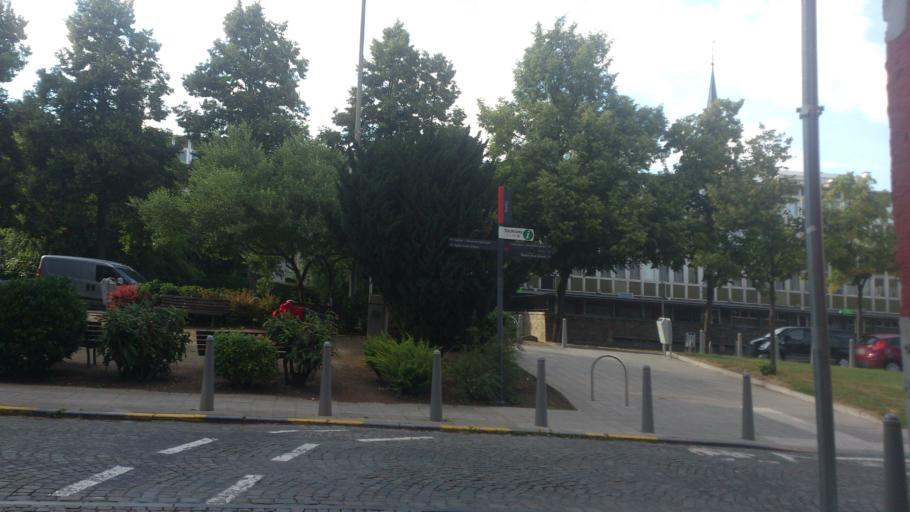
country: BE
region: Wallonia
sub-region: Province de Liege
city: Liege
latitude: 50.6377
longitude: 5.5720
